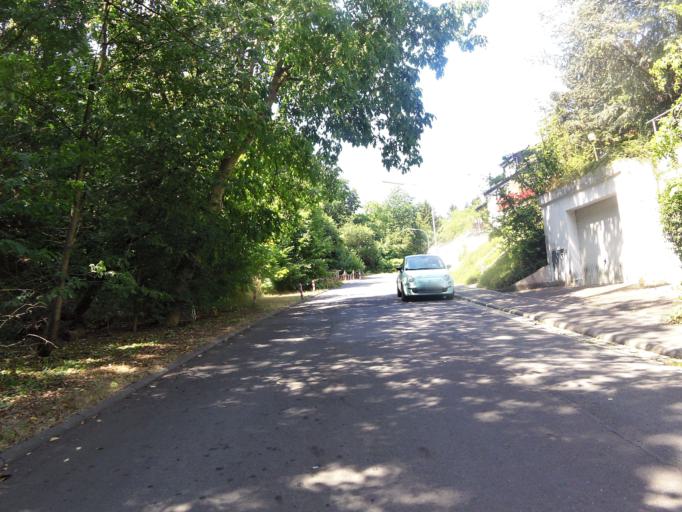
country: DE
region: Bavaria
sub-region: Regierungsbezirk Unterfranken
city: Wuerzburg
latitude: 49.8142
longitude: 9.9520
